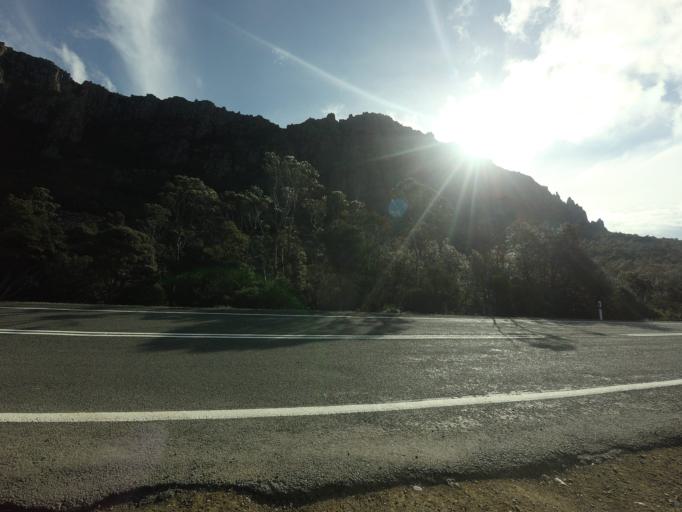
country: AU
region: Tasmania
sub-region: Meander Valley
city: Deloraine
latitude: -41.7208
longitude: 146.7249
